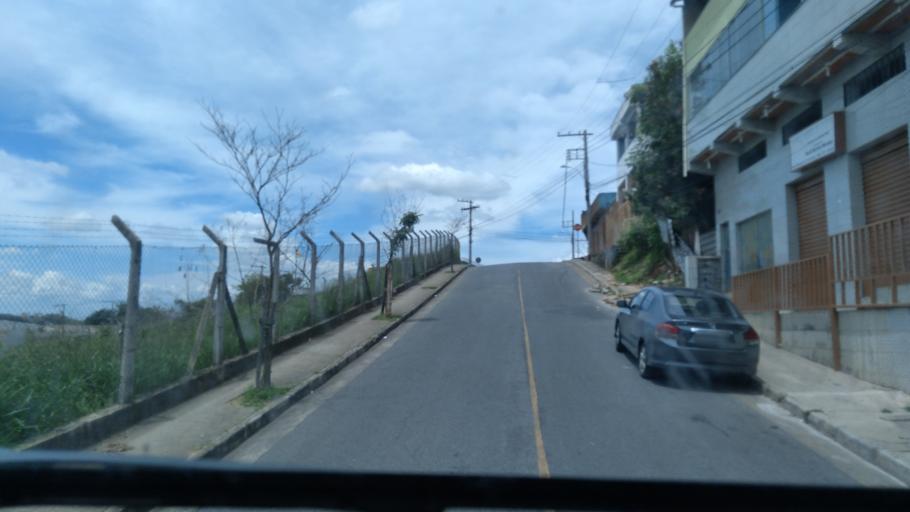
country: BR
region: Minas Gerais
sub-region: Belo Horizonte
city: Belo Horizonte
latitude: -19.9152
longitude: -43.8872
